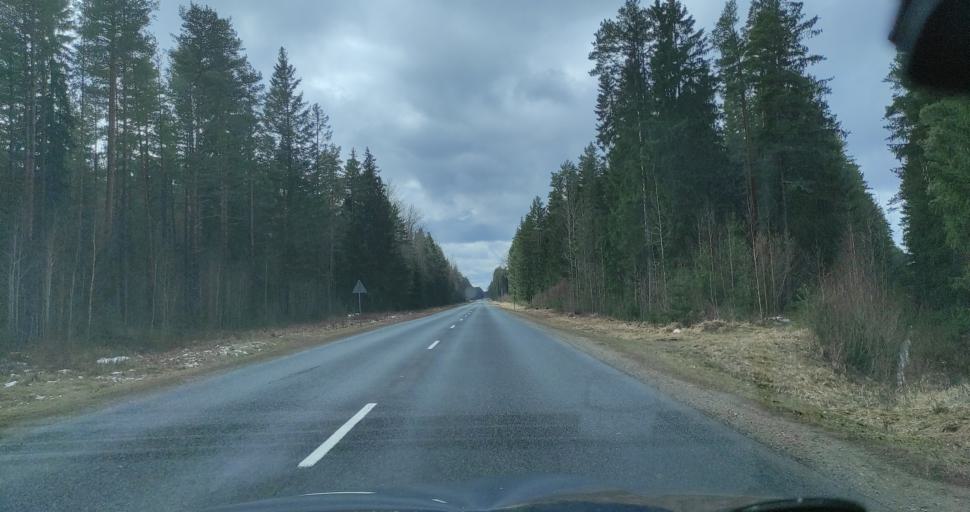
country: LV
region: Talsu Rajons
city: Stende
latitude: 57.1183
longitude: 22.5169
